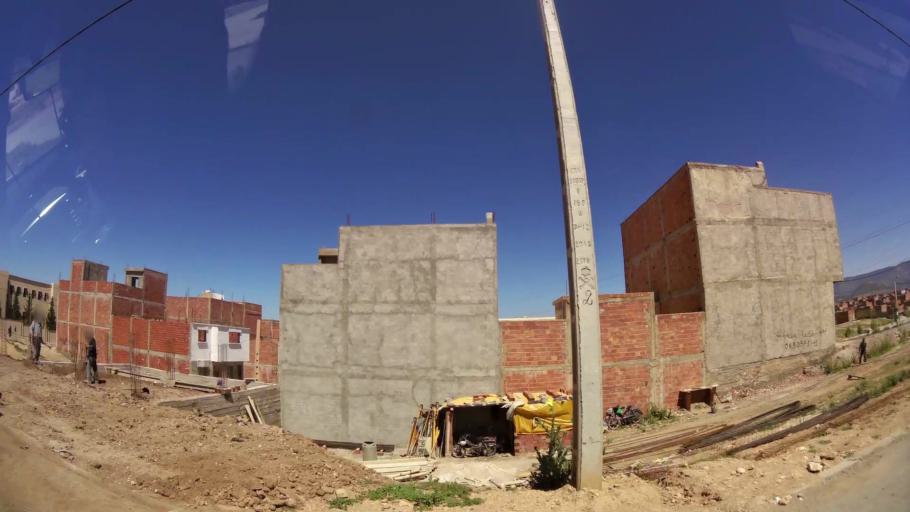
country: MA
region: Oriental
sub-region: Oujda-Angad
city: Oujda
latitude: 34.6570
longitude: -1.8678
